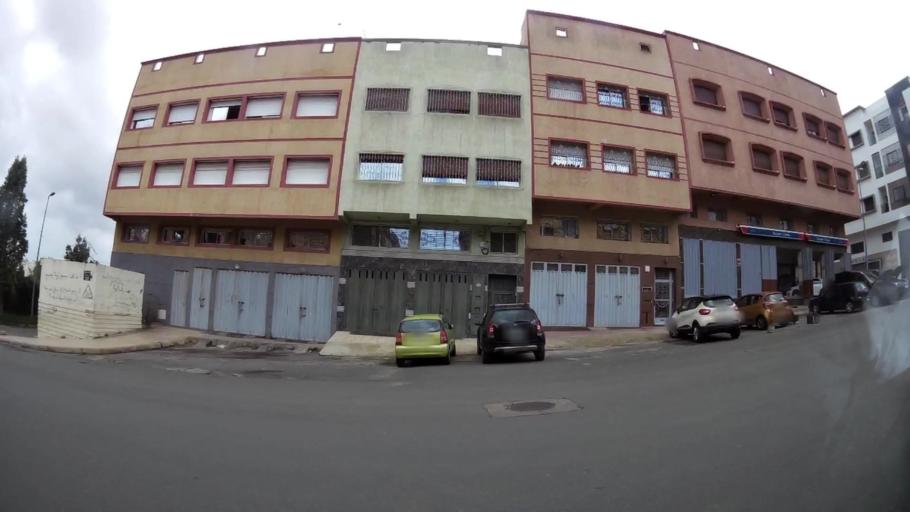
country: MA
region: Grand Casablanca
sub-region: Casablanca
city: Casablanca
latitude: 33.5336
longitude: -7.5889
